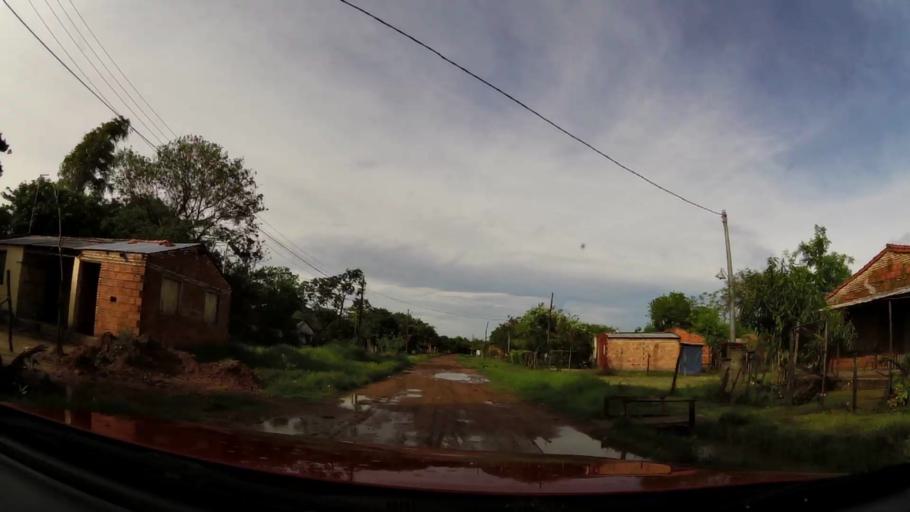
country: PY
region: Central
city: Limpio
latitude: -25.1857
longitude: -57.4805
